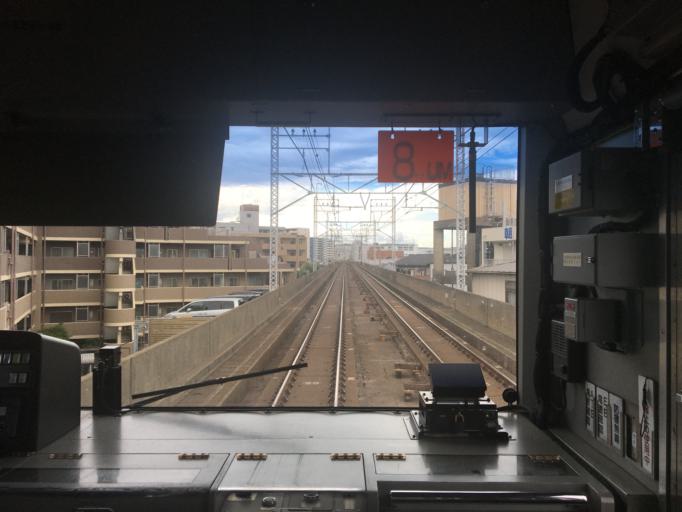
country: JP
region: Saitama
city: Asaka
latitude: 35.8093
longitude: 139.5794
